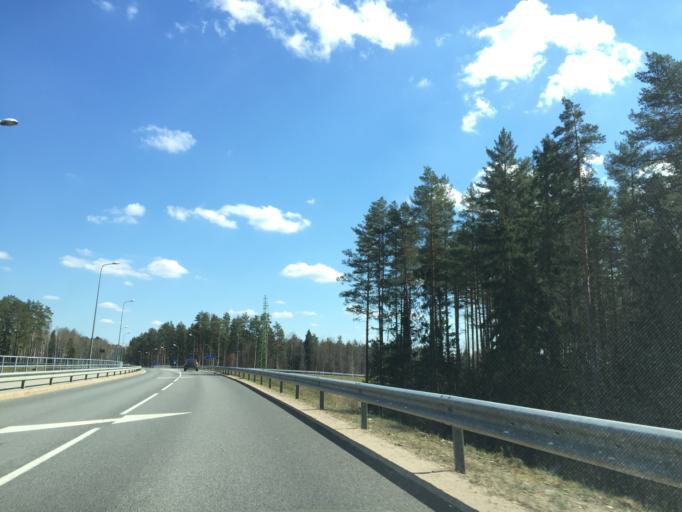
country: LV
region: Saulkrastu
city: Saulkrasti
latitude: 57.2459
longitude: 24.4238
